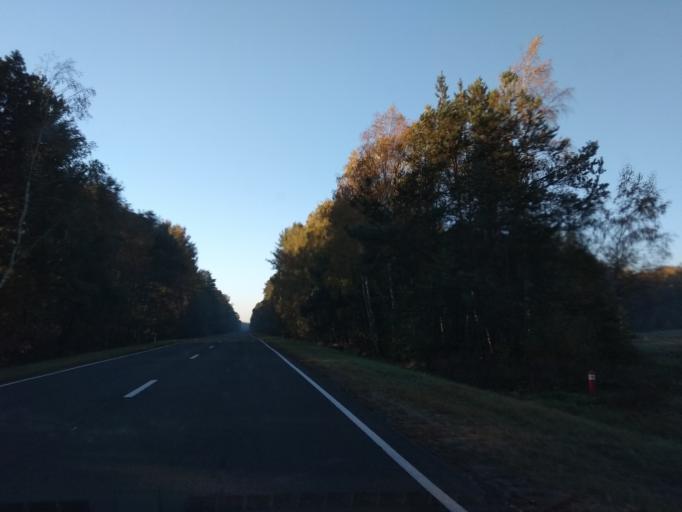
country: BY
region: Brest
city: Kobryn
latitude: 52.0474
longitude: 24.2762
